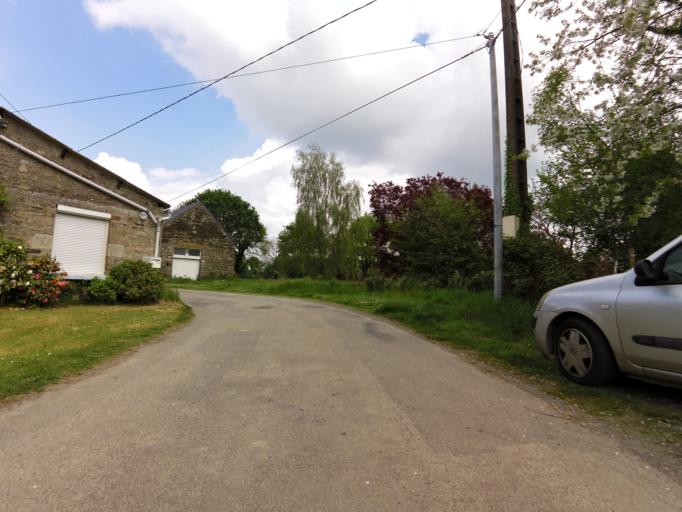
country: FR
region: Brittany
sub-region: Departement du Morbihan
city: Saint-Martin-sur-Oust
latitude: 47.7273
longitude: -2.2746
